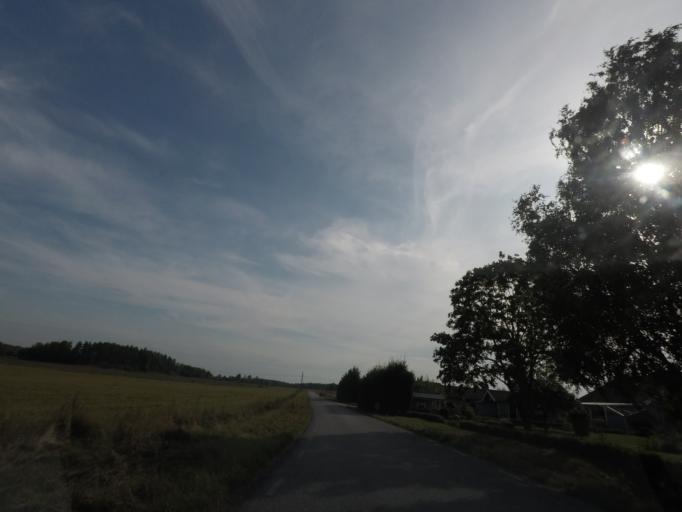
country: SE
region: Vaestmanland
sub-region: Hallstahammars Kommun
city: Kolback
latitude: 59.5327
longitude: 16.1411
